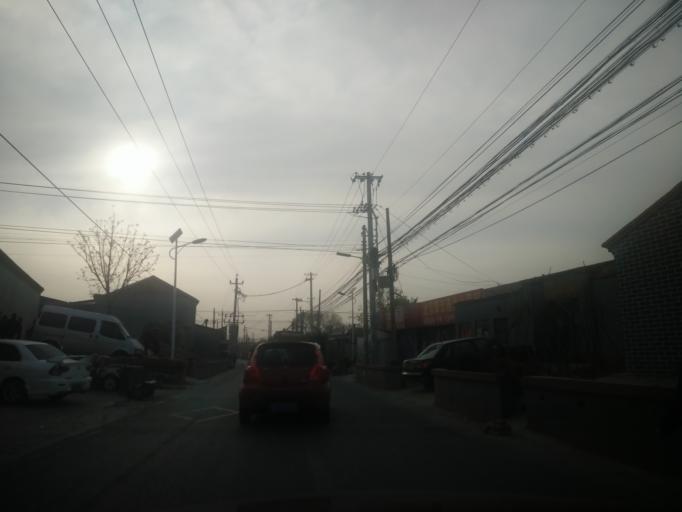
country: CN
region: Beijing
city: Qingyundian
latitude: 39.6789
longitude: 116.4796
